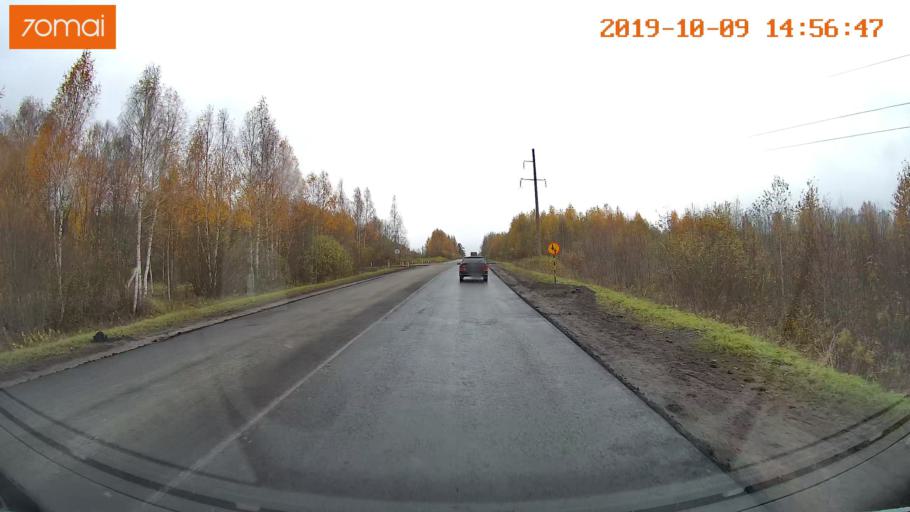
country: RU
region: Kostroma
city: Chistyye Bory
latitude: 58.3432
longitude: 41.6485
